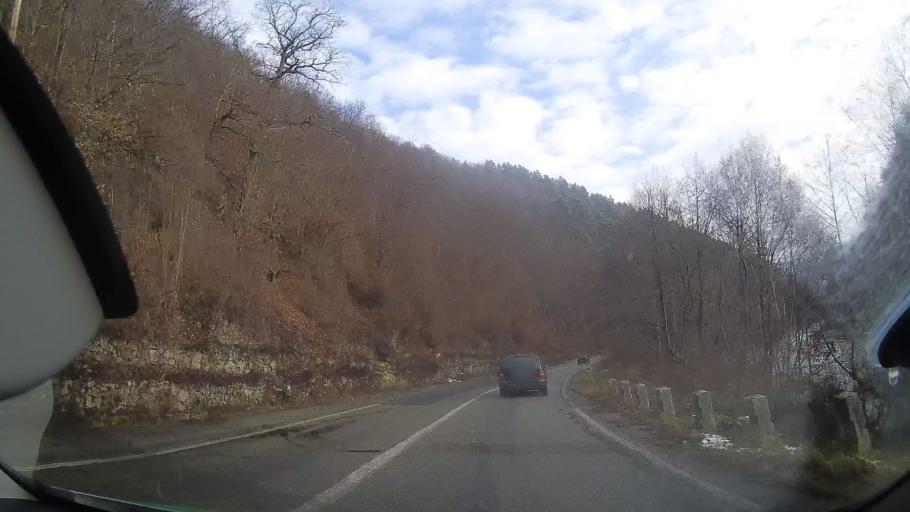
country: RO
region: Alba
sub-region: Oras Baia de Aries
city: Baia de Aries
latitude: 46.3826
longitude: 23.2590
